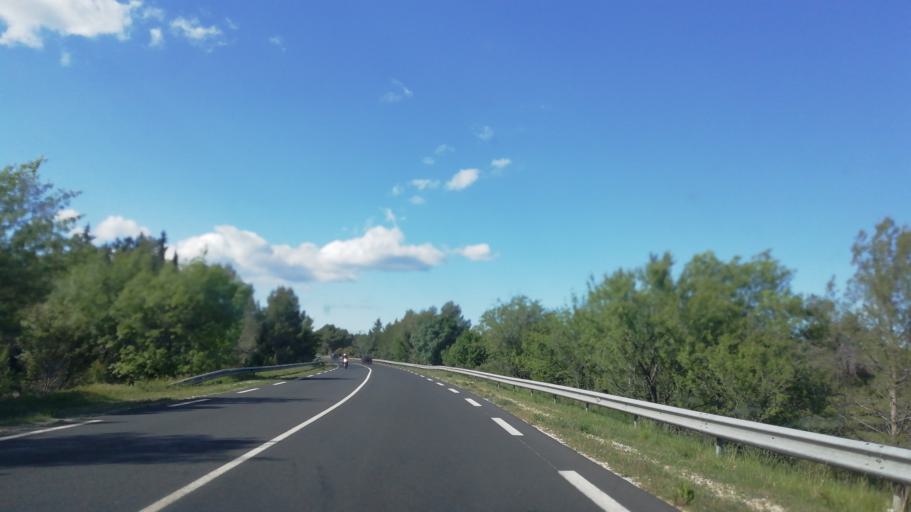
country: FR
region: Languedoc-Roussillon
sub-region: Departement de l'Herault
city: Saint-Clement-de-Riviere
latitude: 43.6941
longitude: 3.8267
